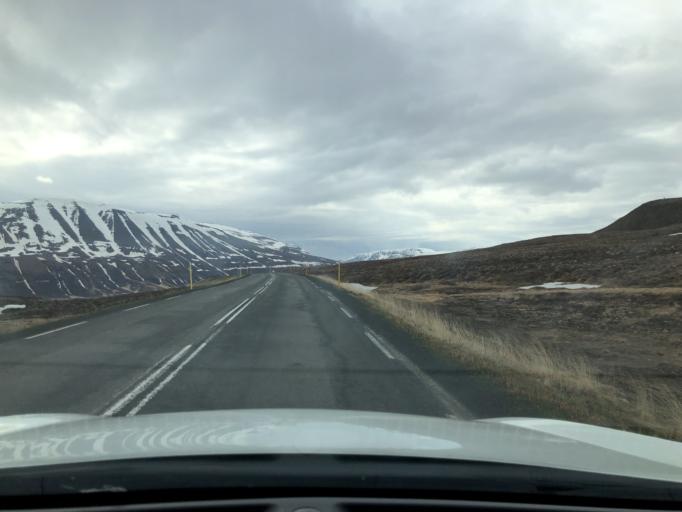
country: IS
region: Northeast
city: Akureyri
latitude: 65.8053
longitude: -17.9610
